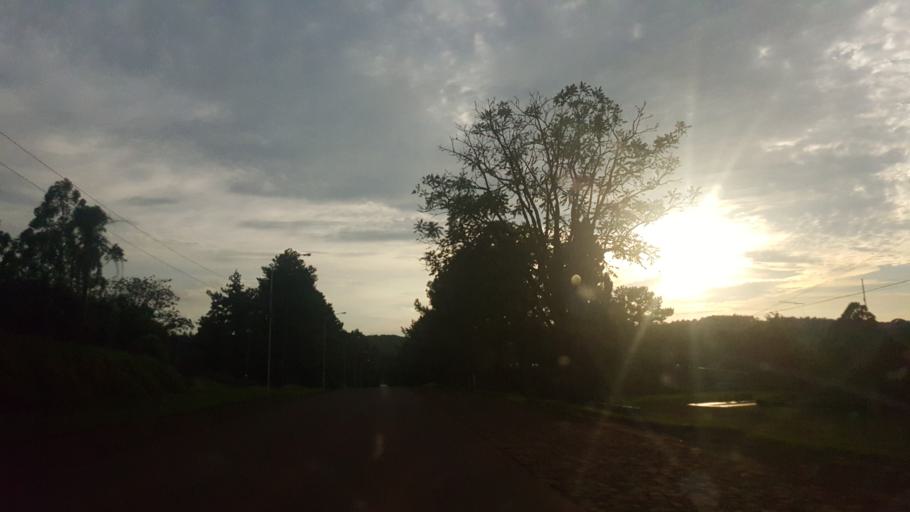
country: AR
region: Misiones
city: Dos de Mayo
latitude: -27.0363
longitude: -54.6820
